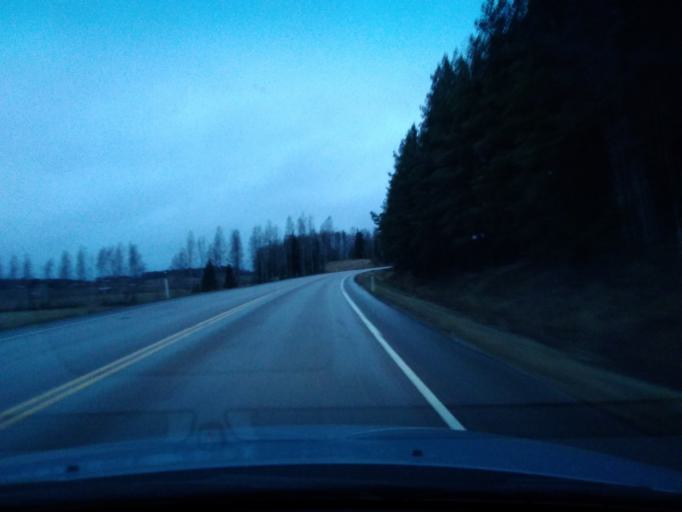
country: FI
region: Uusimaa
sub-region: Porvoo
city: Askola
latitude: 60.4690
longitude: 25.5706
